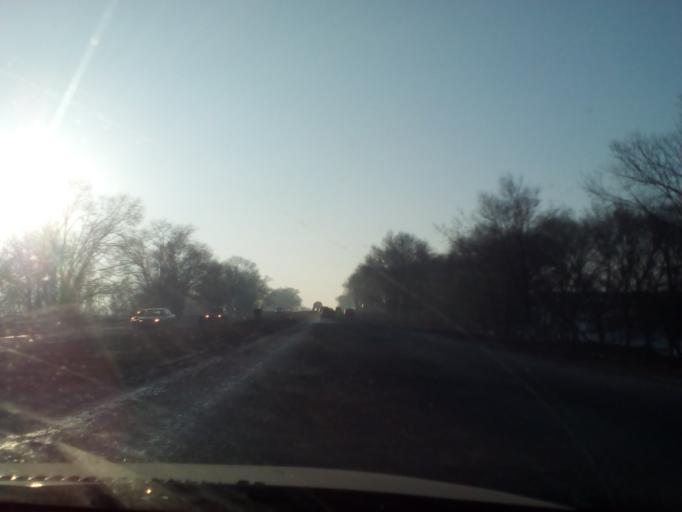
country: KZ
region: Almaty Oblysy
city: Burunday
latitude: 43.2227
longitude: 76.5800
